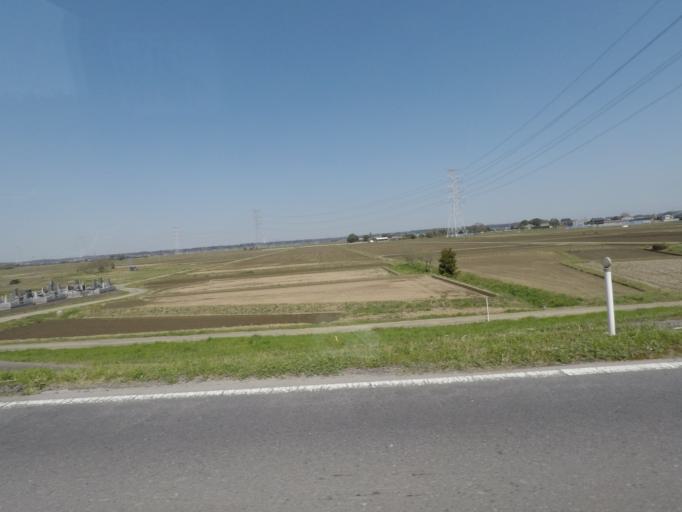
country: JP
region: Ibaraki
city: Inashiki
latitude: 35.9078
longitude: 140.3829
